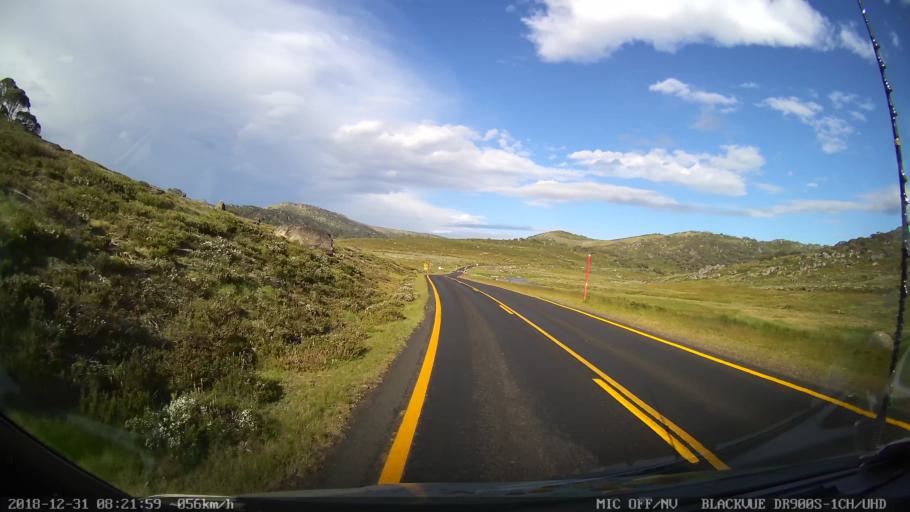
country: AU
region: New South Wales
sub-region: Snowy River
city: Jindabyne
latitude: -36.4290
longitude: 148.3625
